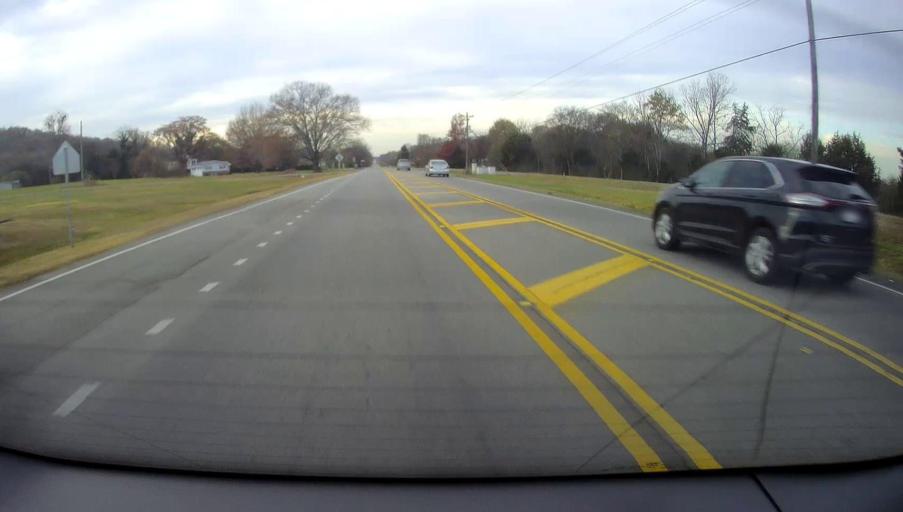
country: US
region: Alabama
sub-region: Morgan County
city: Falkville
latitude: 34.4162
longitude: -86.7051
